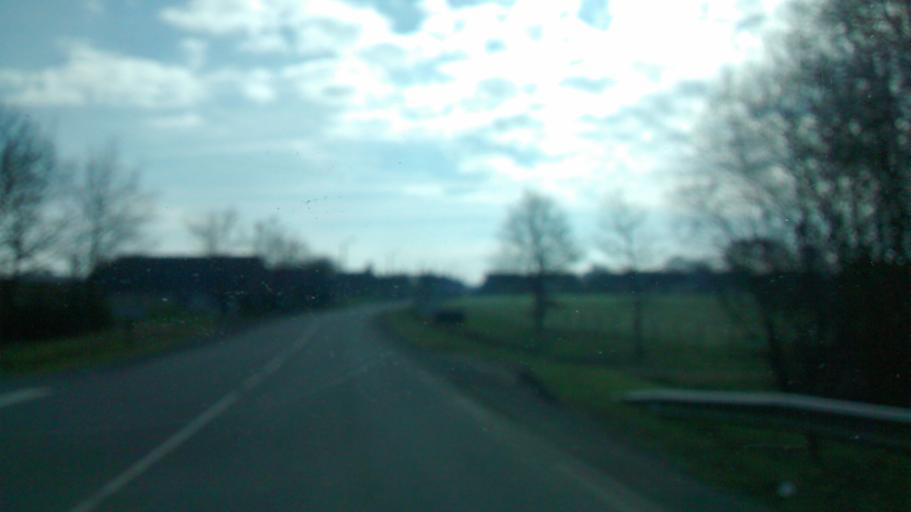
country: FR
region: Brittany
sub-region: Departement d'Ille-et-Vilaine
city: Fouillard
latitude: 48.1628
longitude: -1.5893
